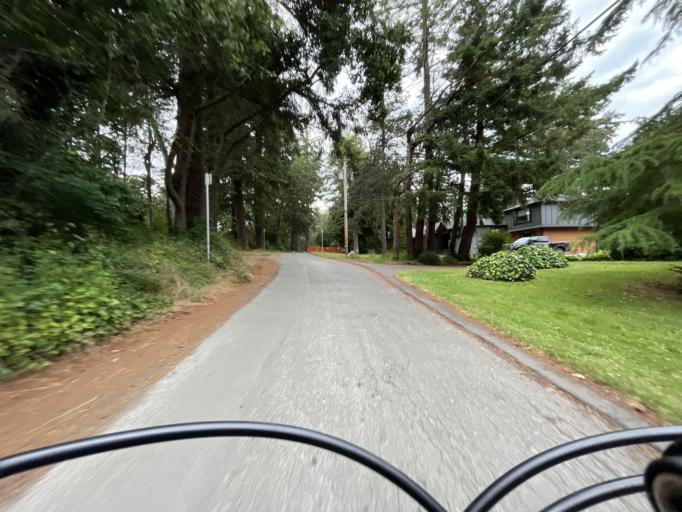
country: CA
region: British Columbia
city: Oak Bay
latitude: 48.4806
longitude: -123.3458
